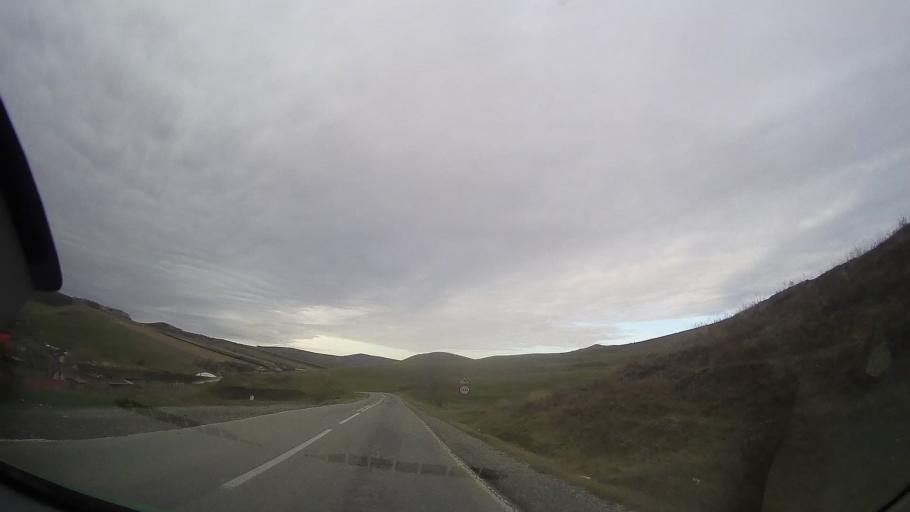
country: RO
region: Mures
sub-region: Comuna Sarmasu
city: Sarmasu
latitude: 46.7954
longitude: 24.1807
